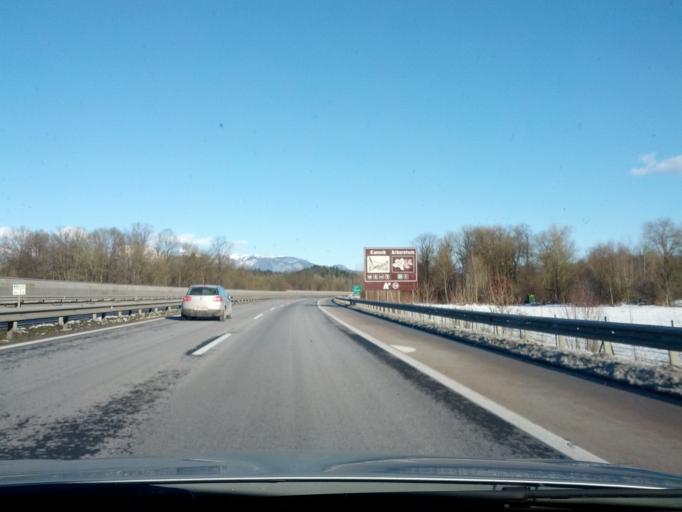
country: SI
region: Domzale
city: Domzale
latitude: 46.1234
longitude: 14.6035
